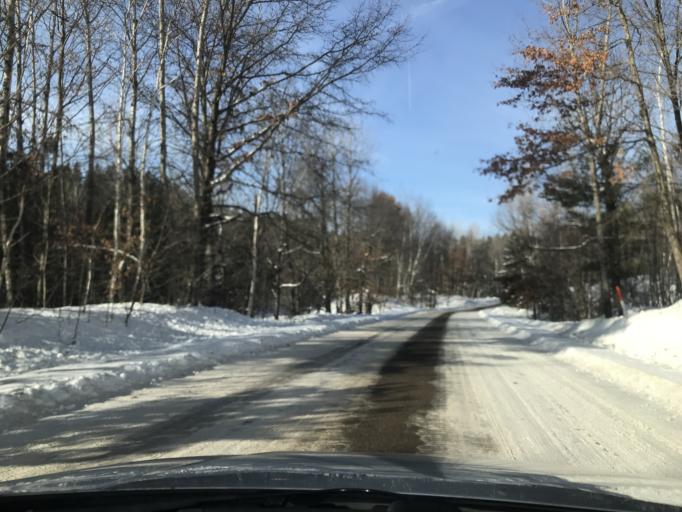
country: US
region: Wisconsin
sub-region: Menominee County
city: Legend Lake
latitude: 45.3232
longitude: -88.5273
